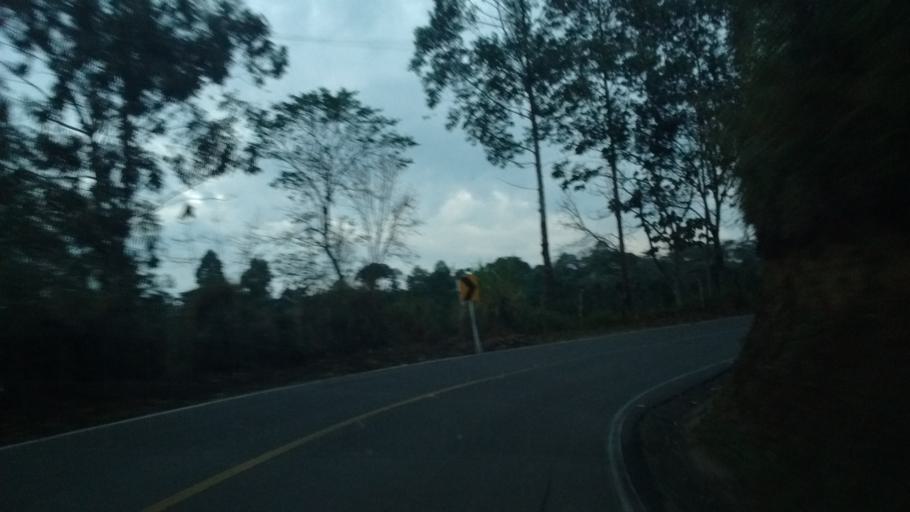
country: CO
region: Cauca
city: Popayan
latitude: 2.3619
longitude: -76.6844
